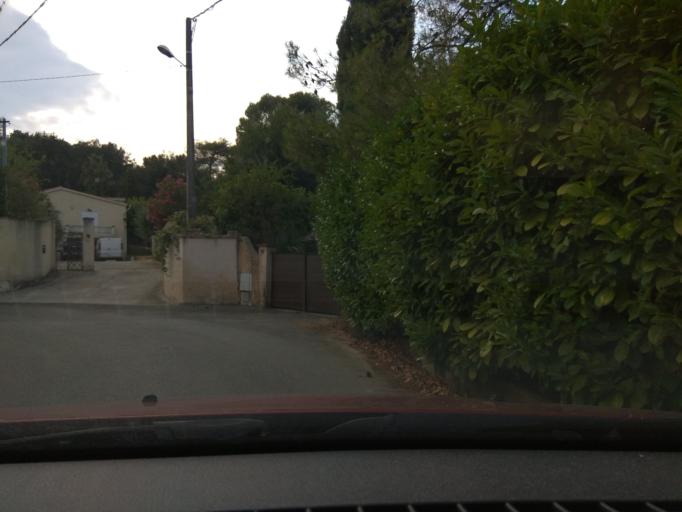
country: FR
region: Provence-Alpes-Cote d'Azur
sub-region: Departement des Alpes-Maritimes
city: Valbonne
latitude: 43.6450
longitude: 7.0304
